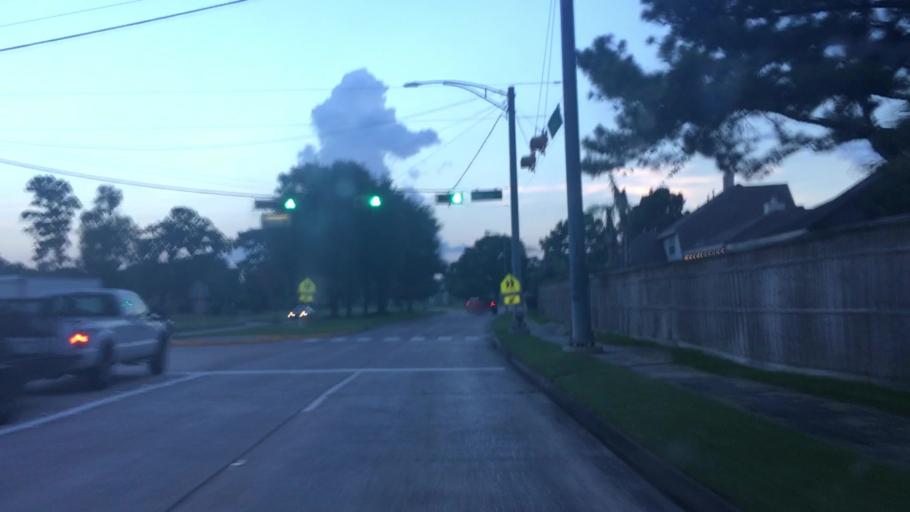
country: US
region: Texas
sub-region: Harris County
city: Atascocita
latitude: 30.0048
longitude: -95.1649
